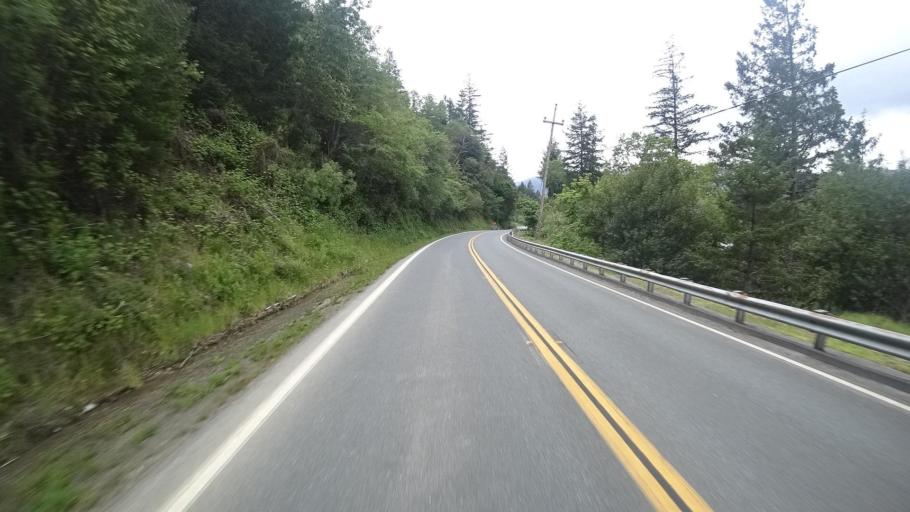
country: US
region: California
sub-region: Humboldt County
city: Willow Creek
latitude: 41.1077
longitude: -123.6868
